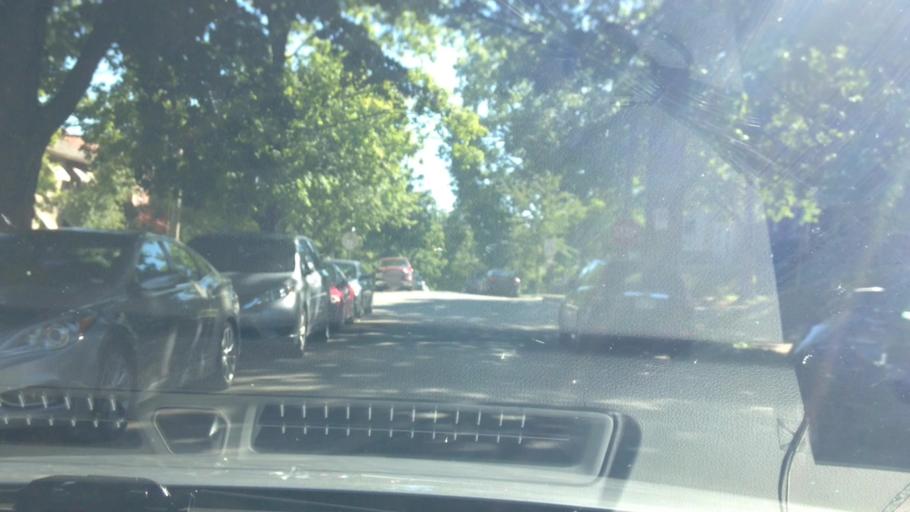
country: US
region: Kansas
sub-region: Johnson County
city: Westwood
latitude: 39.0412
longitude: -94.6009
